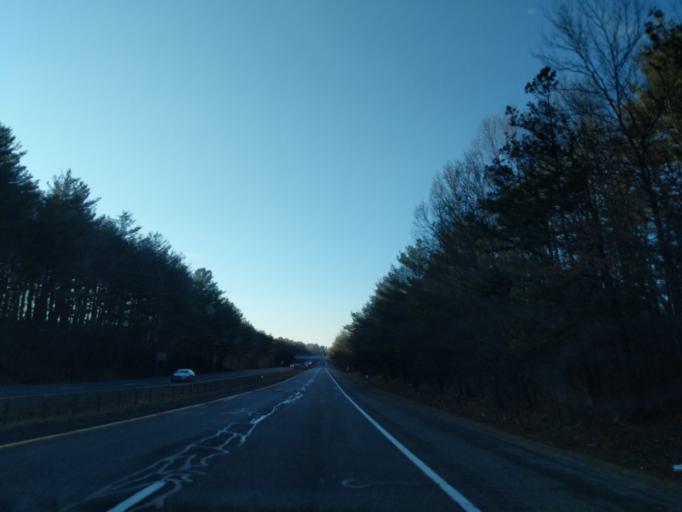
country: US
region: Massachusetts
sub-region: Worcester County
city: Millville
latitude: 42.0105
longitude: -71.5778
